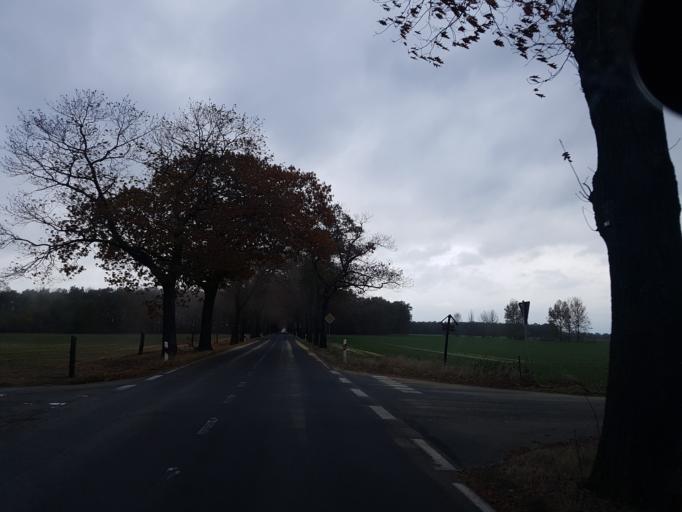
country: DE
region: Brandenburg
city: Herzberg
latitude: 51.6583
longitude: 13.2338
